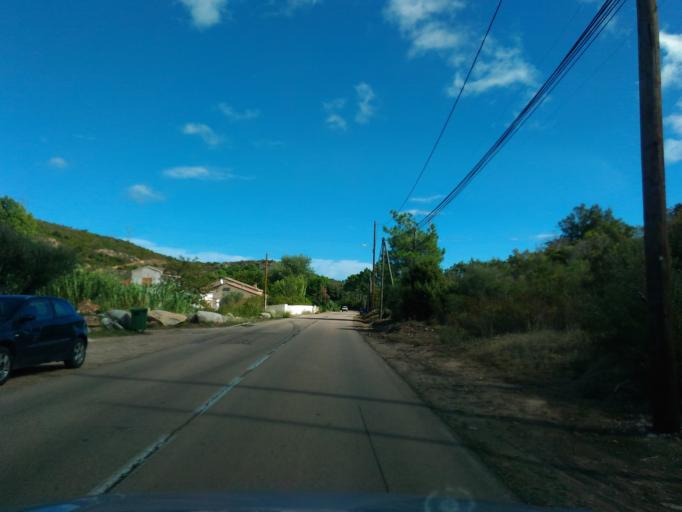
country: FR
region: Corsica
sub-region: Departement de la Corse-du-Sud
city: Porto-Vecchio
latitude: 41.7065
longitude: 9.3284
